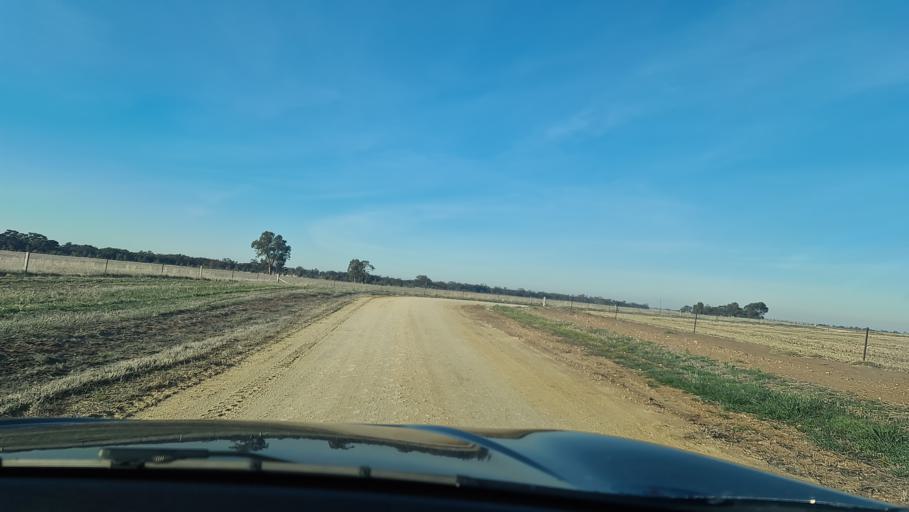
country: AU
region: Victoria
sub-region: Horsham
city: Horsham
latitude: -36.3604
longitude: 142.3965
